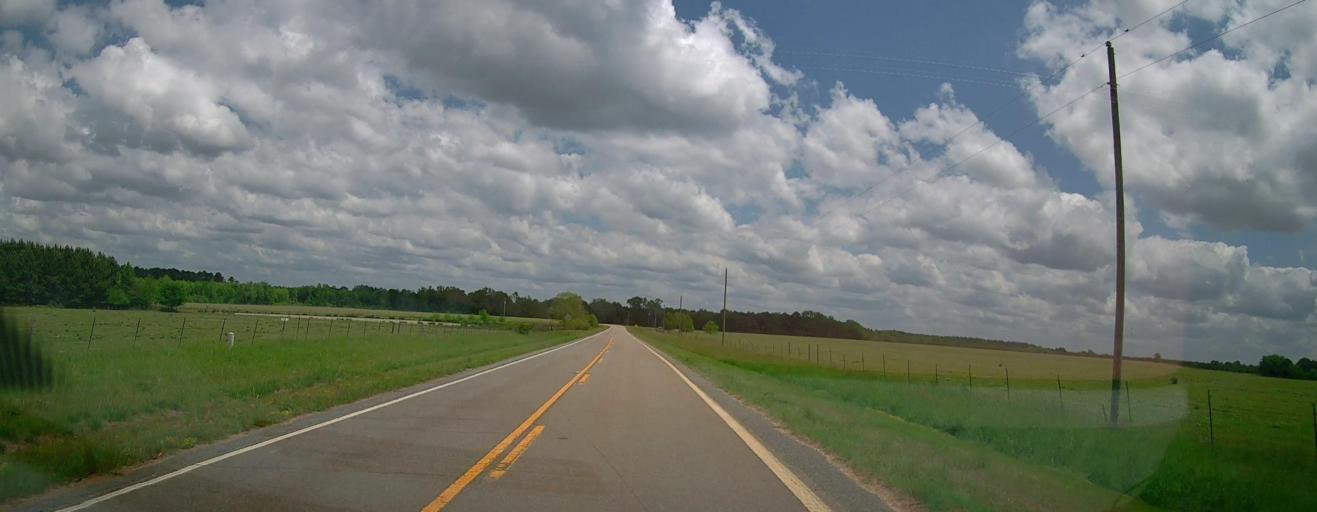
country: US
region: Georgia
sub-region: Dodge County
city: Chester
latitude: 32.5426
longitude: -83.1834
